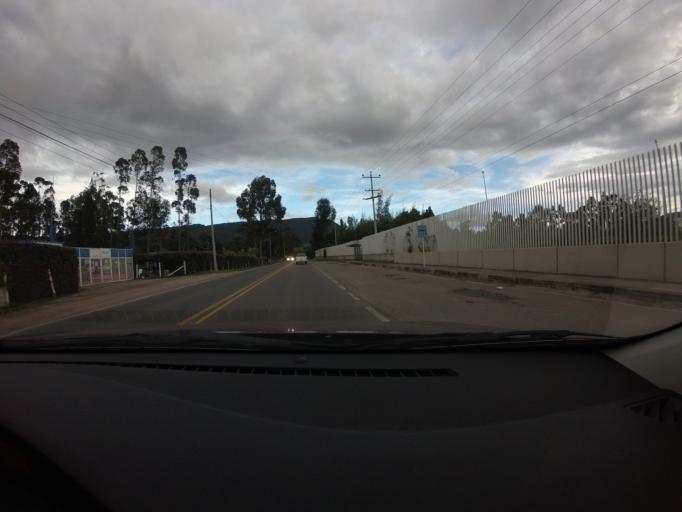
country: CO
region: Cundinamarca
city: Sopo
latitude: 4.9338
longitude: -73.9547
